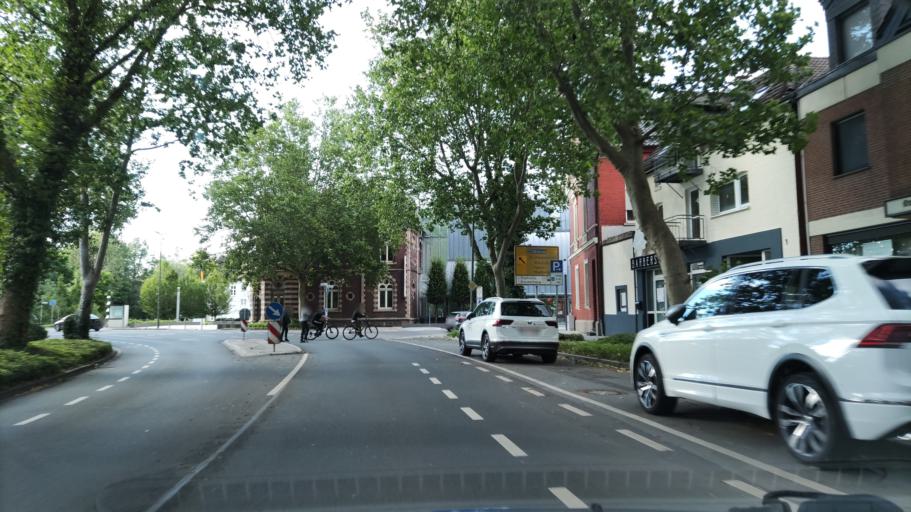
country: DE
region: North Rhine-Westphalia
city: Ahlen
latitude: 51.7626
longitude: 7.8860
